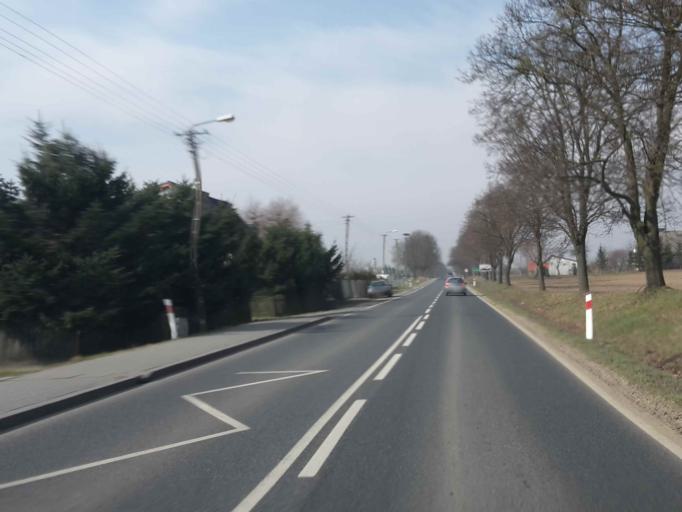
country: PL
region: Kujawsko-Pomorskie
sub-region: Powiat nakielski
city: Szubin
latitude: 53.0721
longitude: 17.7130
